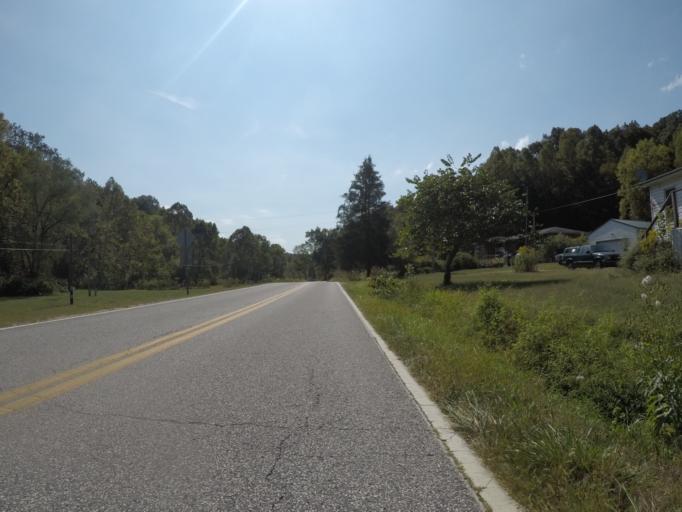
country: US
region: West Virginia
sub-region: Cabell County
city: Lesage
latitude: 38.5632
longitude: -82.3957
